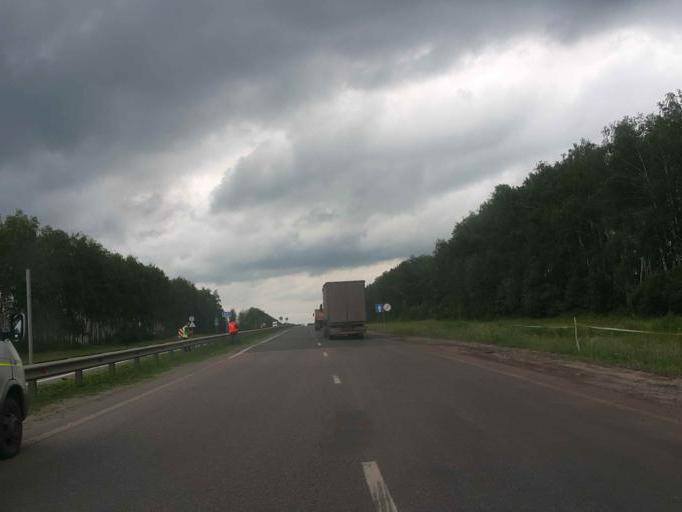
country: RU
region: Tambov
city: Selezni
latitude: 52.7689
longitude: 41.0622
